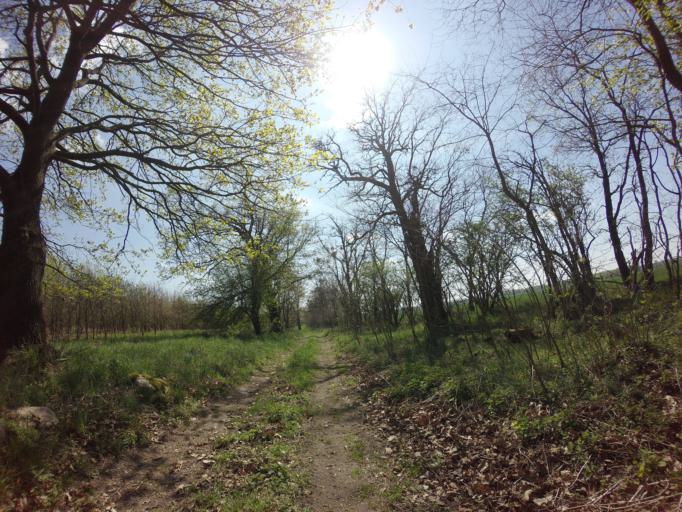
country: PL
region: West Pomeranian Voivodeship
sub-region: Powiat stargardzki
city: Suchan
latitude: 53.2118
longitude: 15.3034
